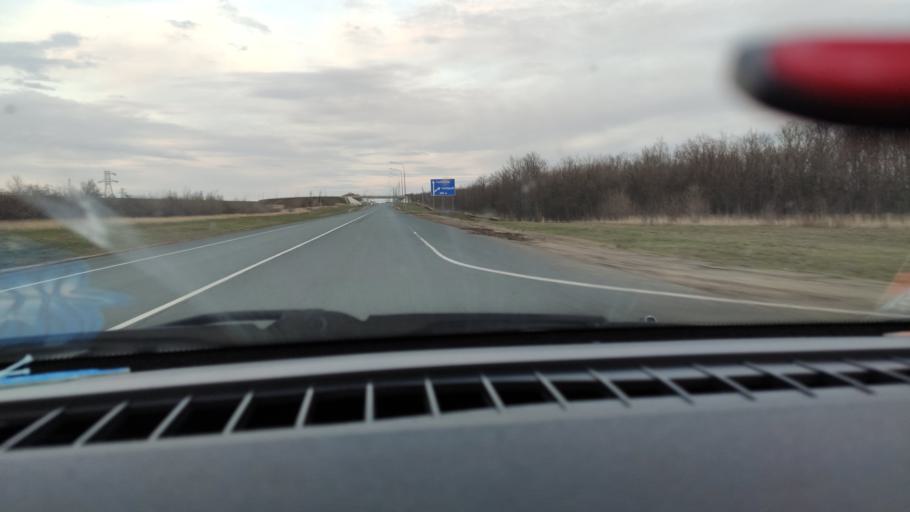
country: RU
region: Saratov
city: Yelshanka
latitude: 51.8253
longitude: 46.2928
